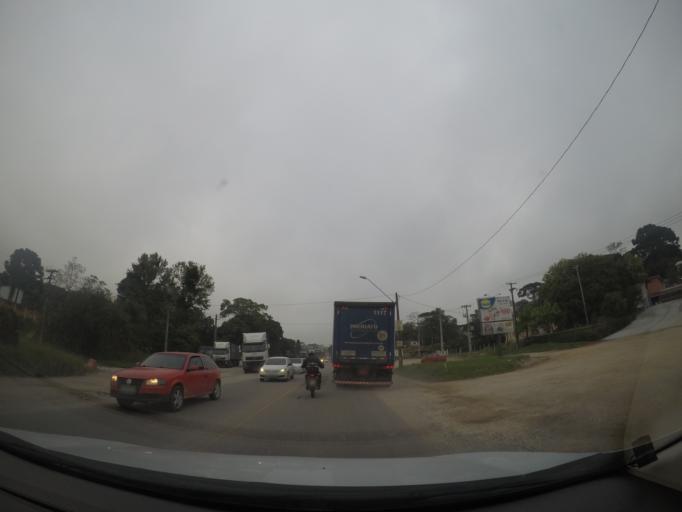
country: BR
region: Parana
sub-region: Almirante Tamandare
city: Almirante Tamandare
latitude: -25.3555
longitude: -49.2809
